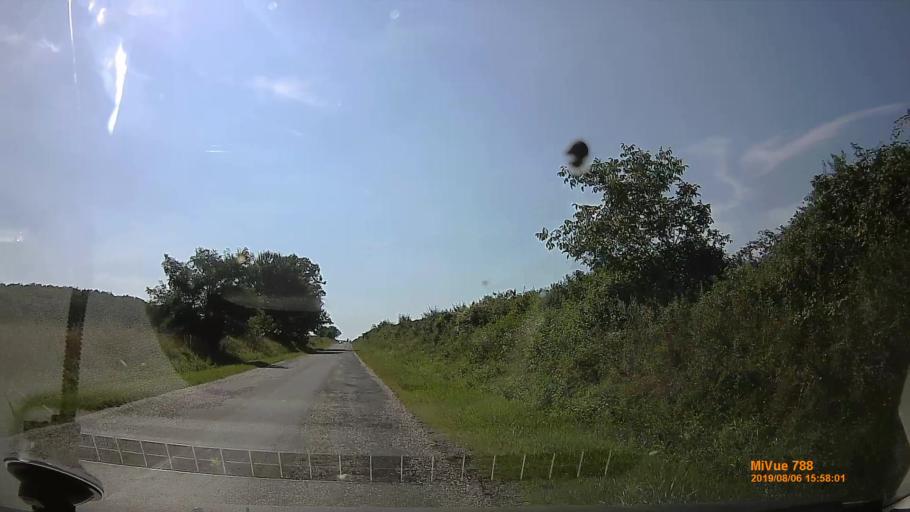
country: HU
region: Somogy
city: Csurgo
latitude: 46.2939
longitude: 16.9980
